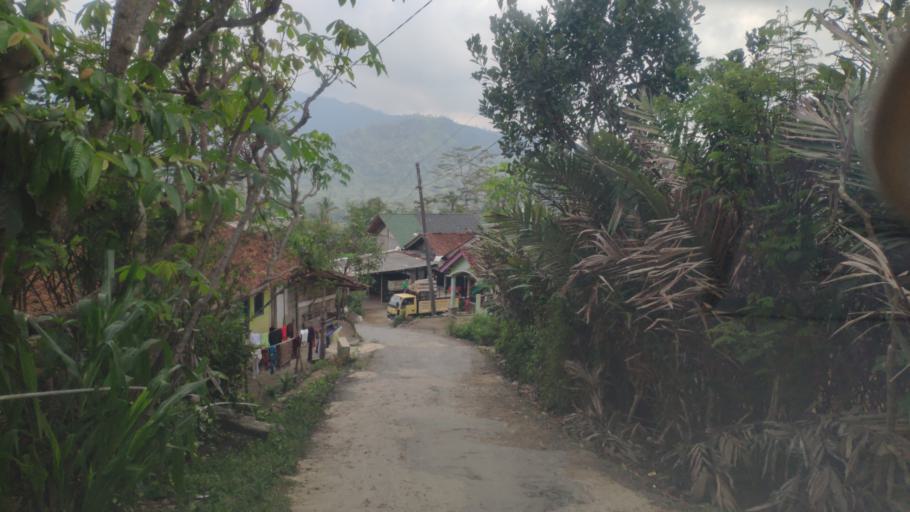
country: ID
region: Central Java
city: Wonosobo
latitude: -7.3387
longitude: 109.7748
